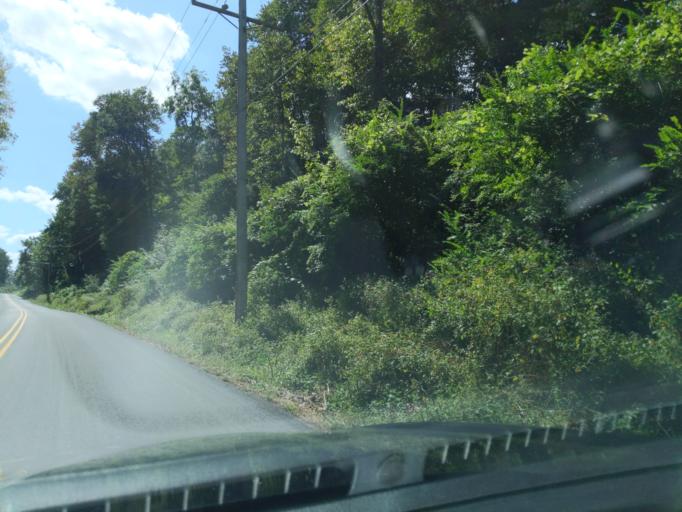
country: US
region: Pennsylvania
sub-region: Blair County
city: Tyrone
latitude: 40.6508
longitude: -78.2116
